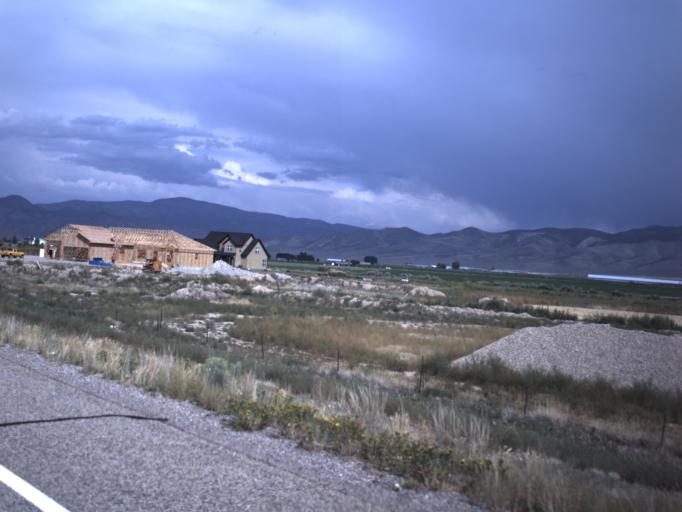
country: US
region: Utah
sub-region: Piute County
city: Junction
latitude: 38.1580
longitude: -112.2804
